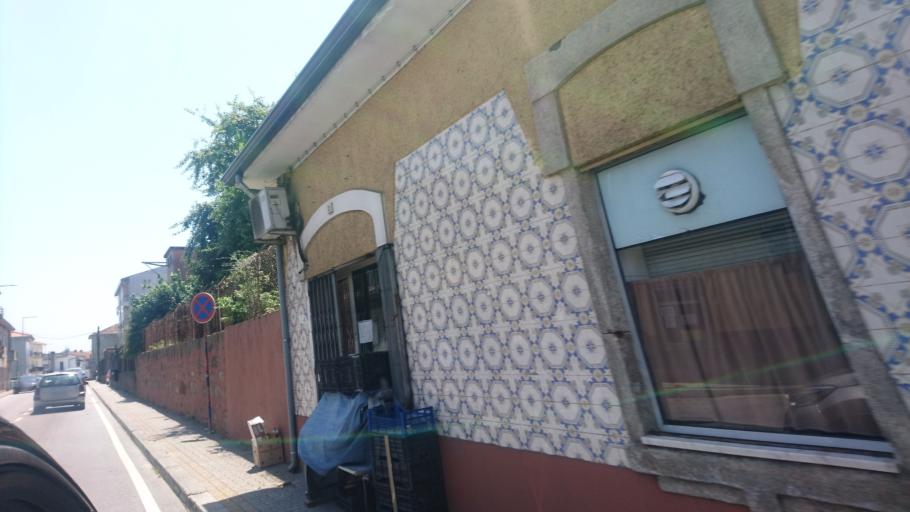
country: PT
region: Porto
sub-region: Gondomar
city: Rio Tinto
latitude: 41.1665
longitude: -8.5472
